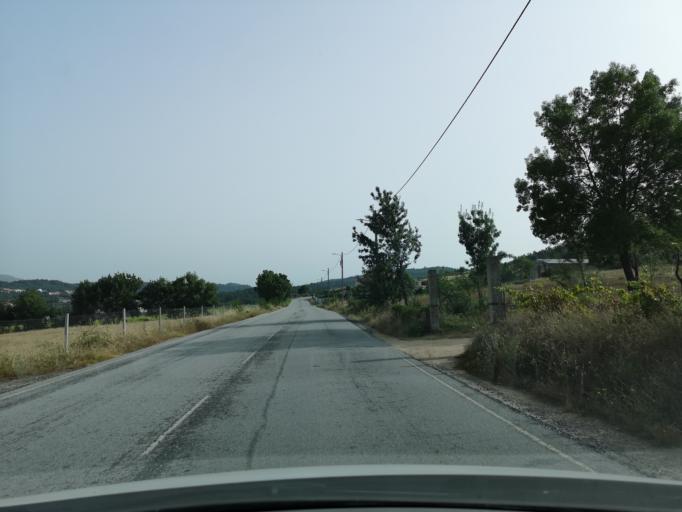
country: PT
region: Castelo Branco
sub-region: Belmonte
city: Belmonte
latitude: 40.3681
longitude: -7.3336
